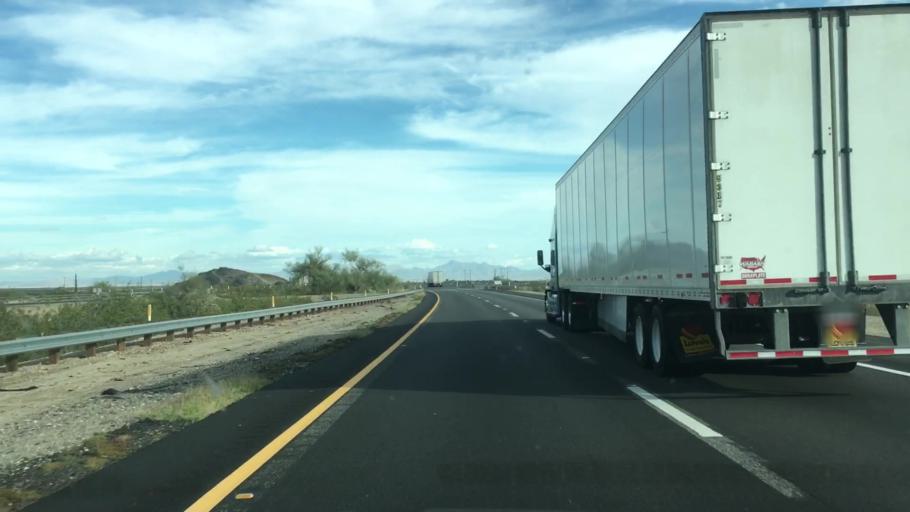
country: US
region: California
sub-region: Riverside County
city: Mesa Verde
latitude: 33.6088
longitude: -114.7715
